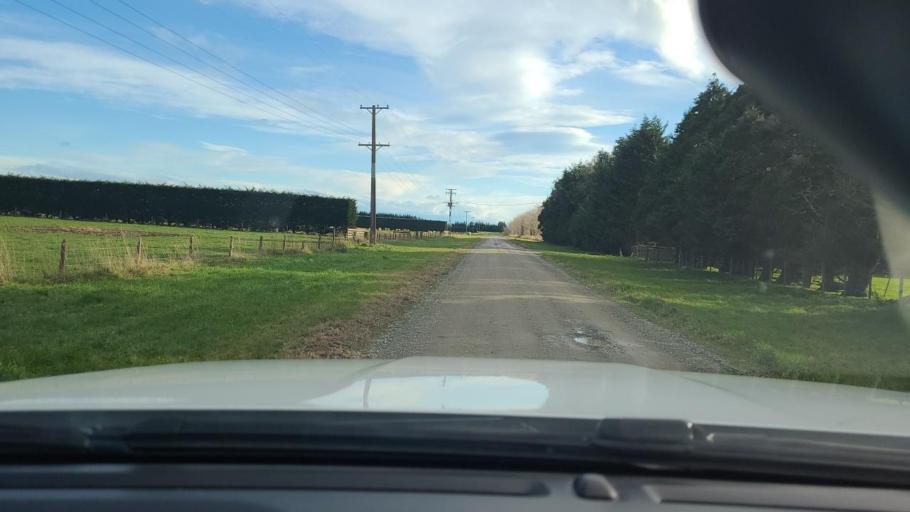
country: NZ
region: Southland
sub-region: Invercargill City
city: Invercargill
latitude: -46.3217
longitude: 168.3007
